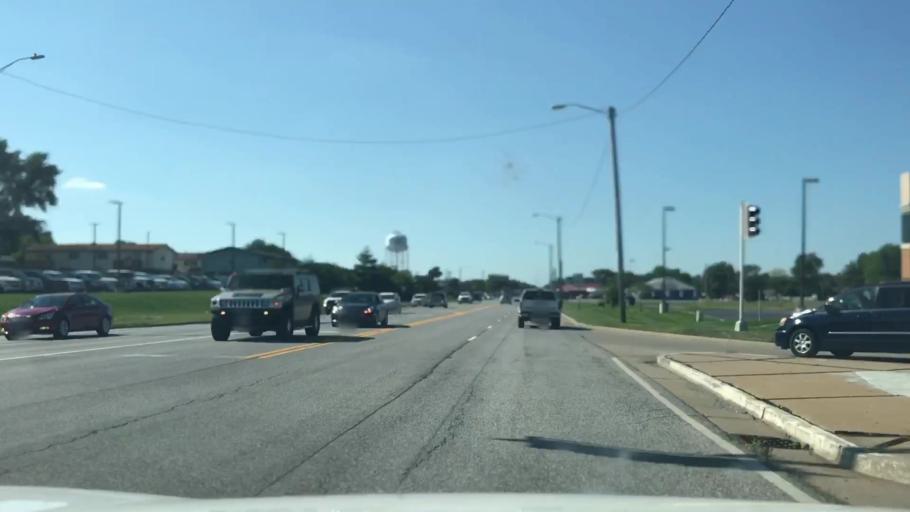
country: US
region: Illinois
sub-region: Madison County
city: Roxana
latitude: 38.8584
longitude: -90.0682
